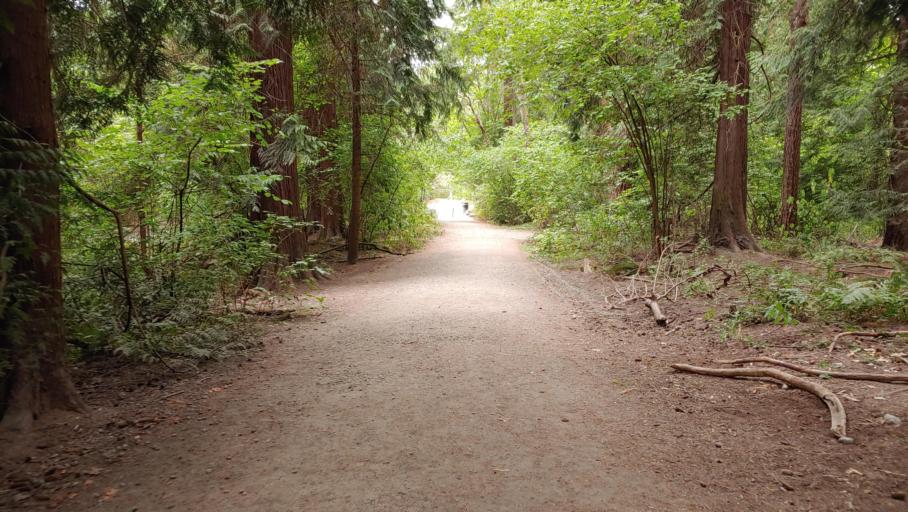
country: US
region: Washington
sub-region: King County
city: Mercer Island
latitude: 47.5533
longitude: -122.2504
